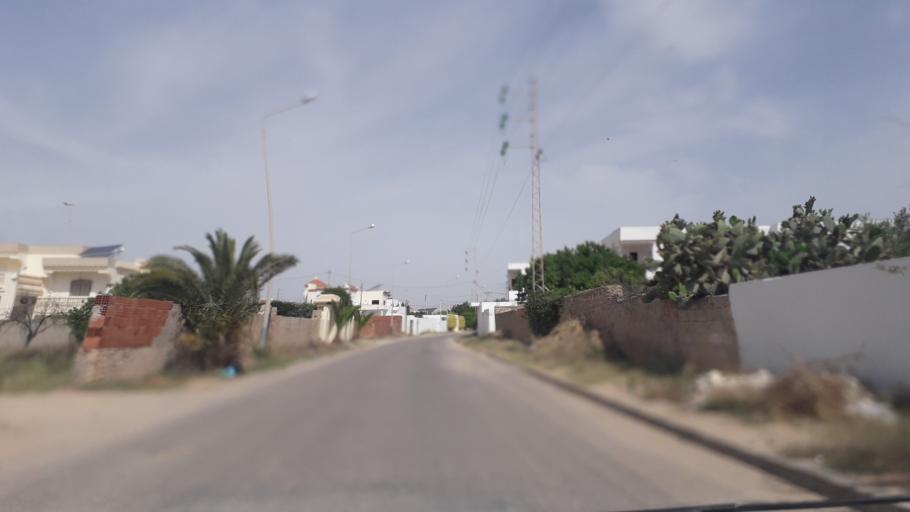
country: TN
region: Safaqis
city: Al Qarmadah
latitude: 34.8057
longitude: 10.7678
